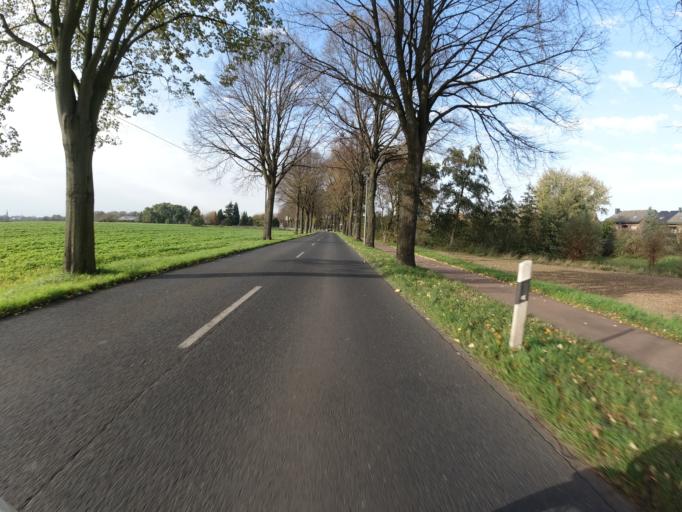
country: DE
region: North Rhine-Westphalia
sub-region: Regierungsbezirk Dusseldorf
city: Moers
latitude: 51.3916
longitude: 6.6766
